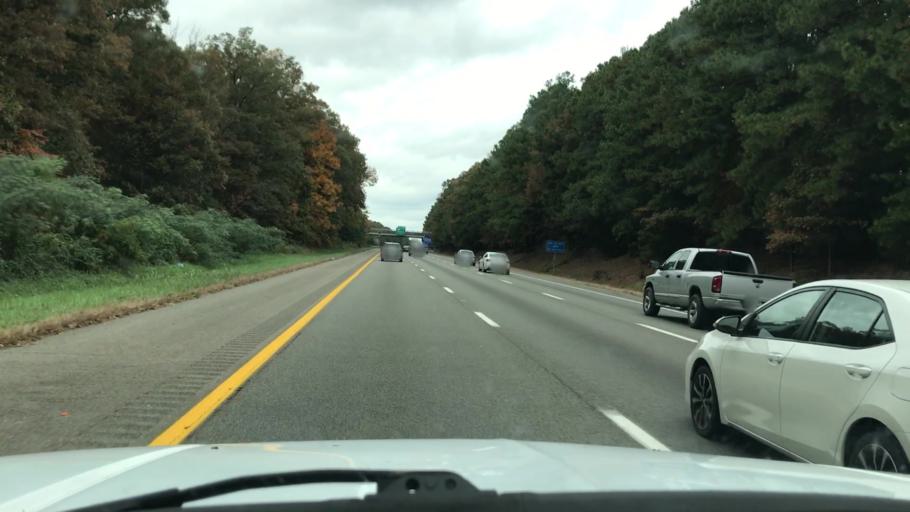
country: US
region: Virginia
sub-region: Henrico County
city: Short Pump
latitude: 37.6399
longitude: -77.5823
